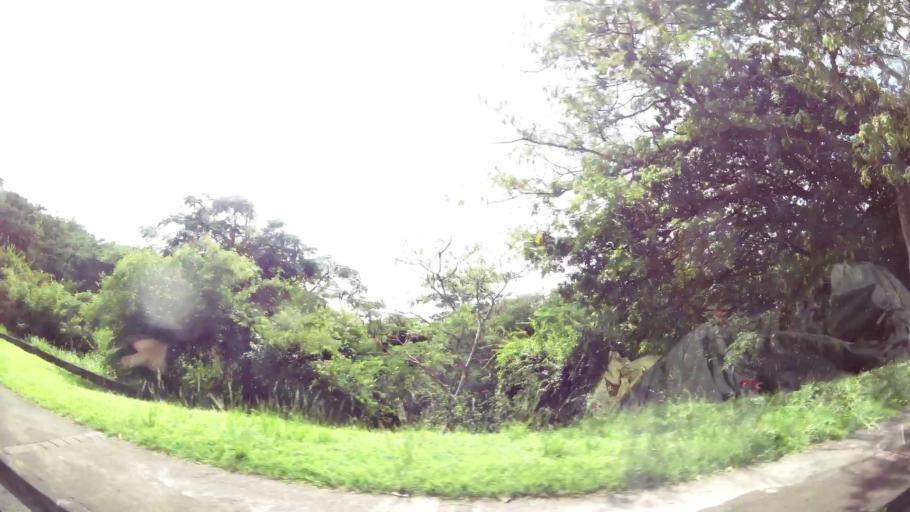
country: GP
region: Guadeloupe
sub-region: Guadeloupe
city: Basse-Terre
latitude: 16.0020
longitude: -61.7260
